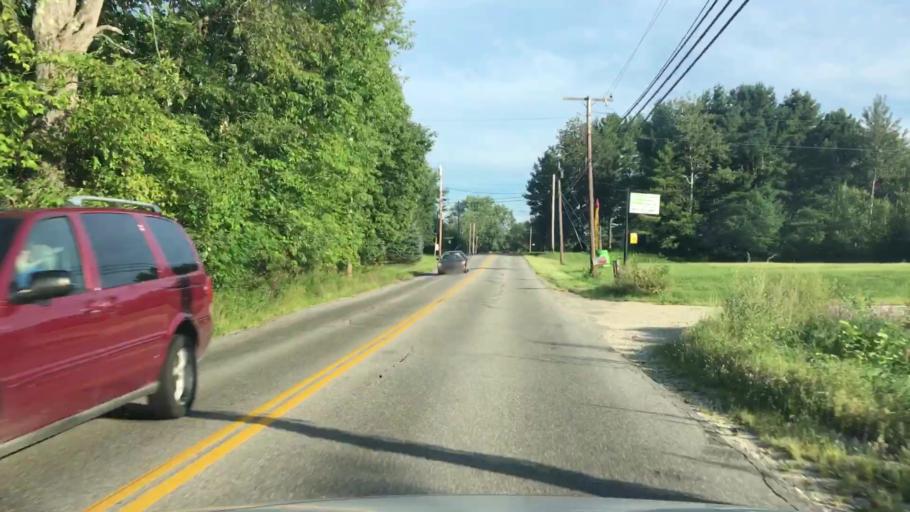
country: US
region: Maine
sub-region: Cumberland County
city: South Windham
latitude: 43.7262
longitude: -70.4058
